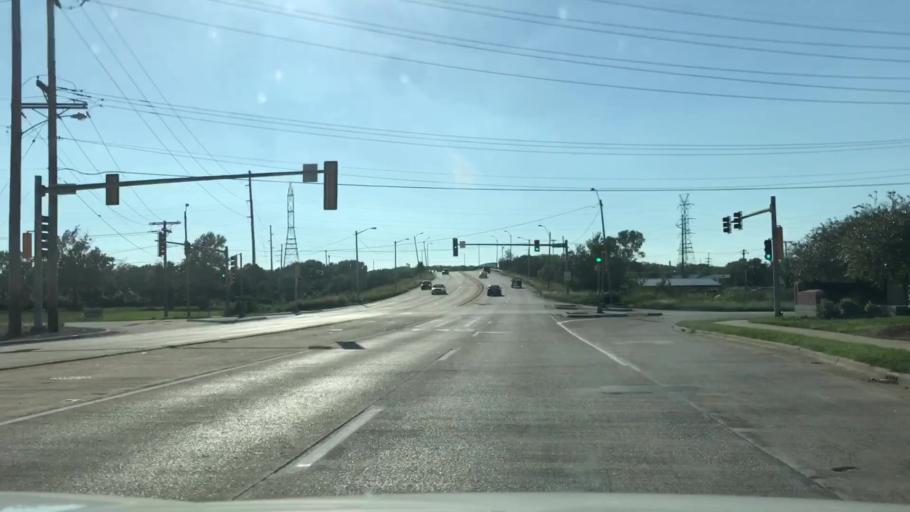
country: US
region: Illinois
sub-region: Madison County
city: Wood River
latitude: 38.8601
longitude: -90.0998
